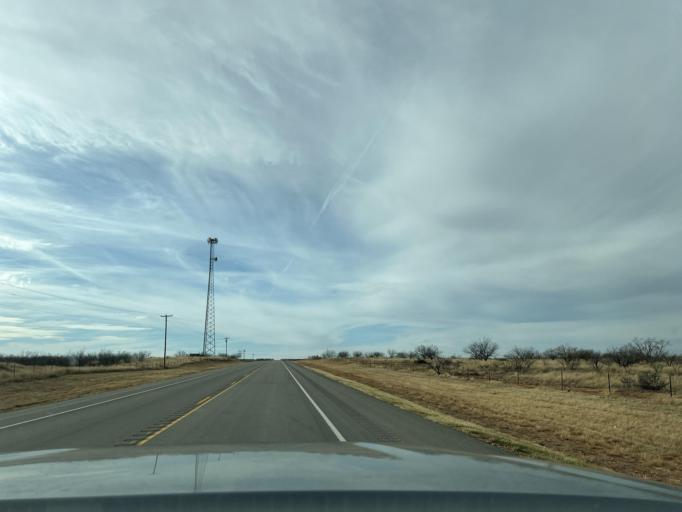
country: US
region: Texas
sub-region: Jones County
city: Anson
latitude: 32.7508
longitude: -99.7226
